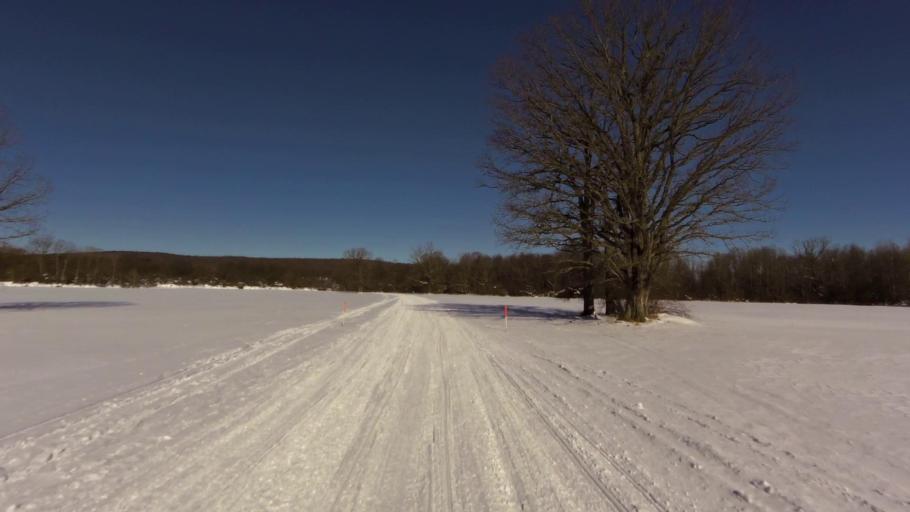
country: US
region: New York
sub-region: Cattaraugus County
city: Franklinville
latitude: 42.3615
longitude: -78.4581
